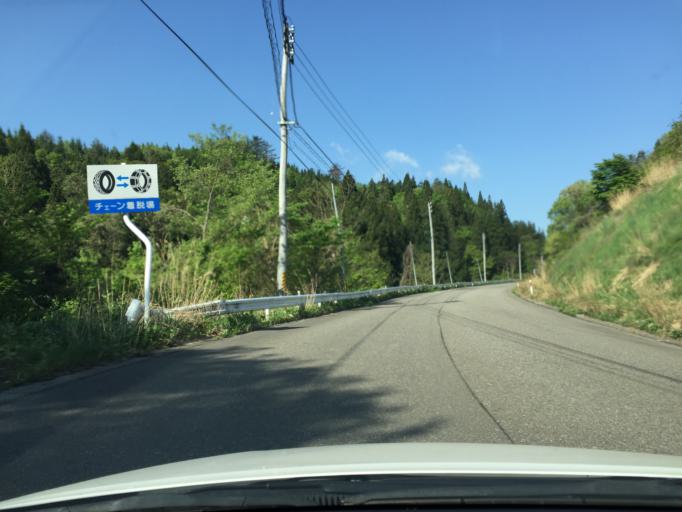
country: JP
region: Fukushima
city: Kitakata
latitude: 37.6729
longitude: 139.6345
